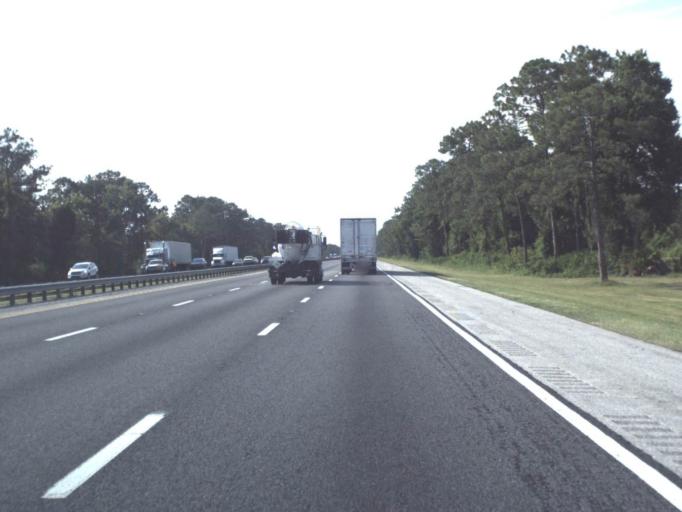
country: US
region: Florida
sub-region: Saint Johns County
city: Saint Augustine Shores
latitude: 29.7694
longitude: -81.3550
